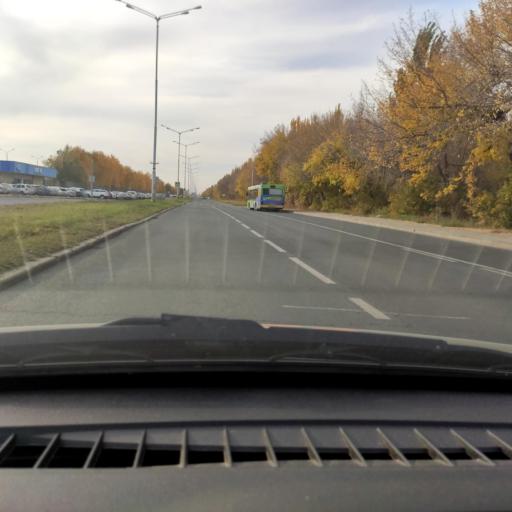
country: RU
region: Samara
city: Tol'yatti
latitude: 53.5706
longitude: 49.2458
